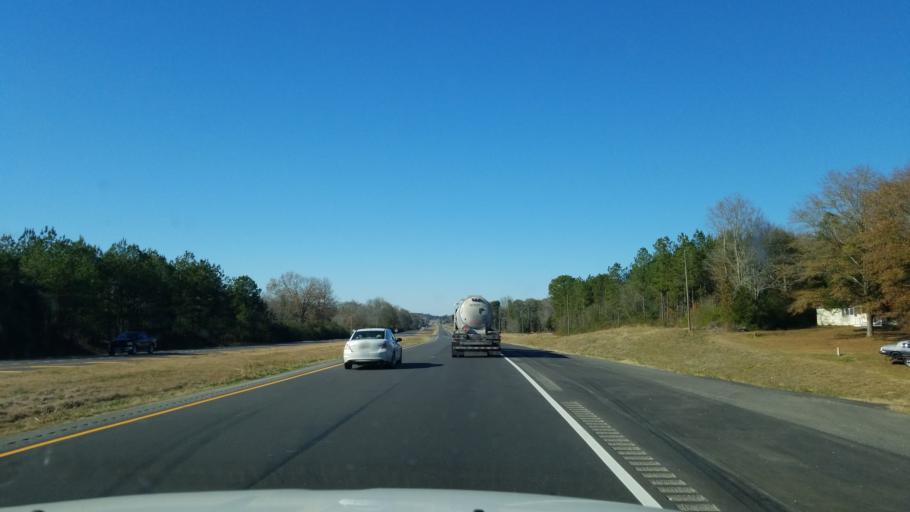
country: US
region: Alabama
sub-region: Pickens County
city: Gordo
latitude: 33.3384
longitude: -87.9353
